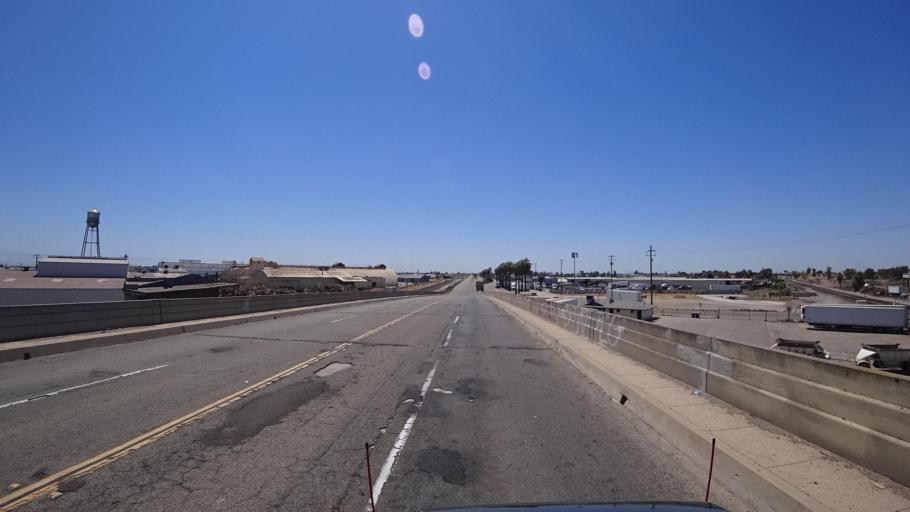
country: US
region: California
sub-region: Fresno County
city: Easton
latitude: 36.6920
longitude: -119.7497
